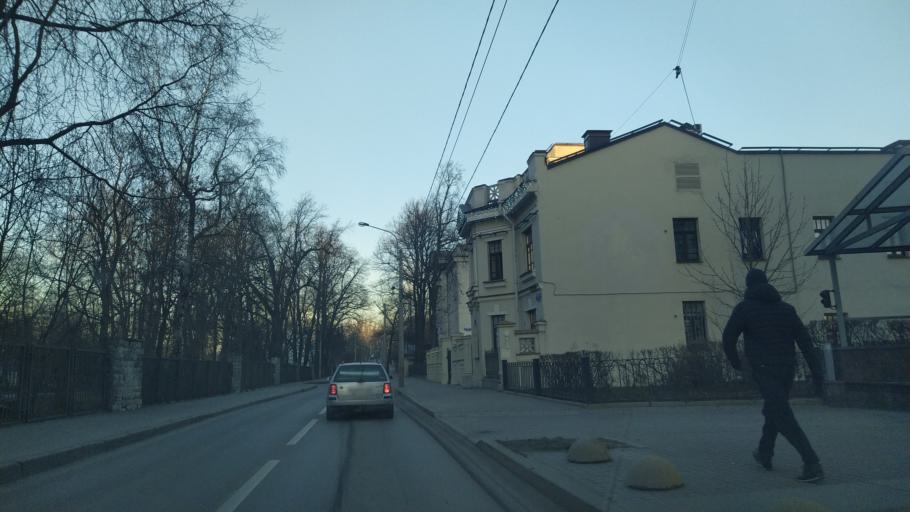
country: RU
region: St.-Petersburg
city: Novaya Derevnya
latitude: 59.9716
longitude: 30.2811
